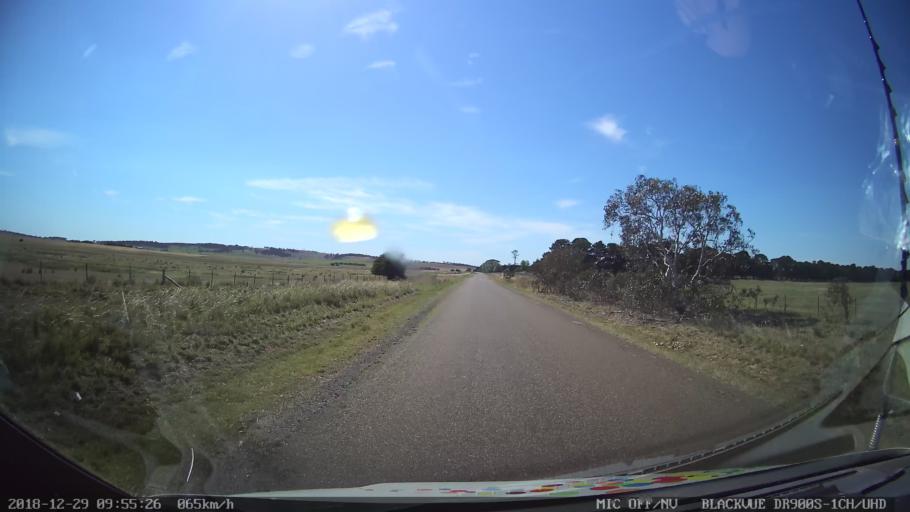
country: AU
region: New South Wales
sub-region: Goulburn Mulwaree
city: Goulburn
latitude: -34.7718
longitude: 149.4682
